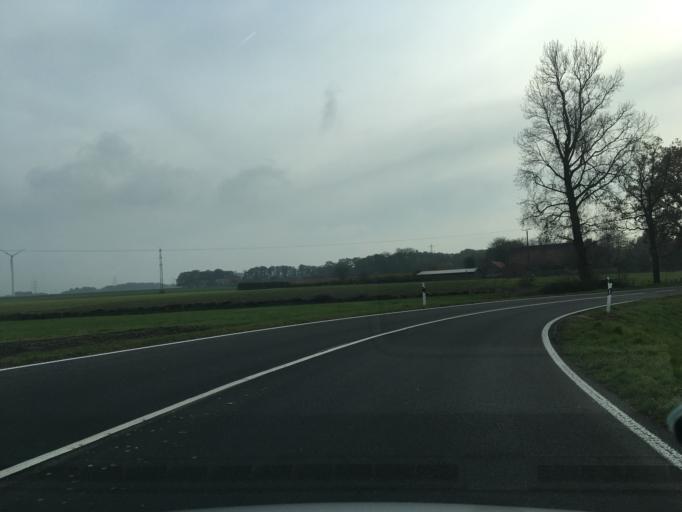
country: DE
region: North Rhine-Westphalia
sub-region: Regierungsbezirk Munster
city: Velen
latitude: 51.9345
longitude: 6.9459
